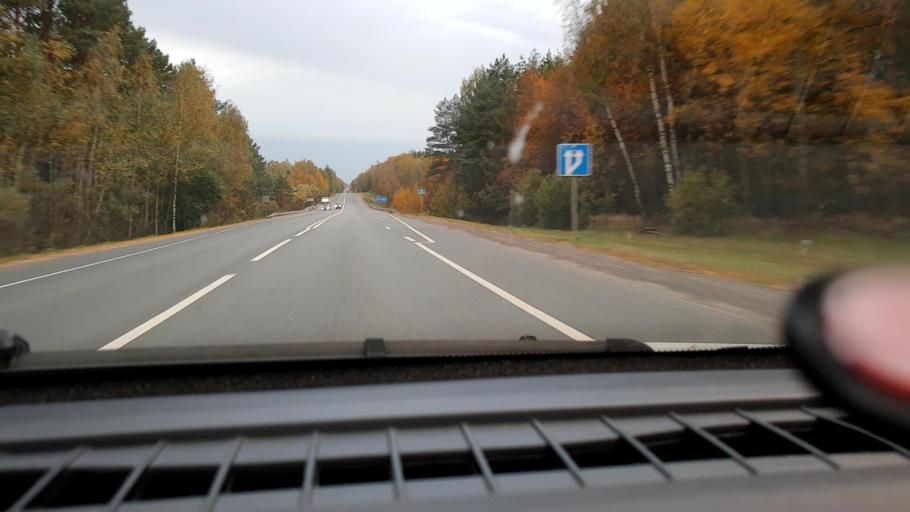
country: RU
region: Vladimir
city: Orgtrud
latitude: 56.2005
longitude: 40.8059
